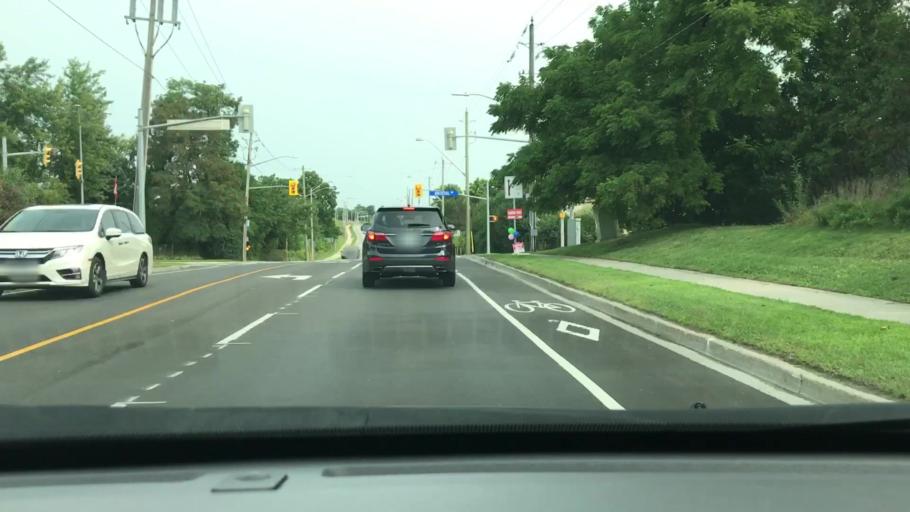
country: CA
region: Ontario
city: Newmarket
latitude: 44.0732
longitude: -79.4591
